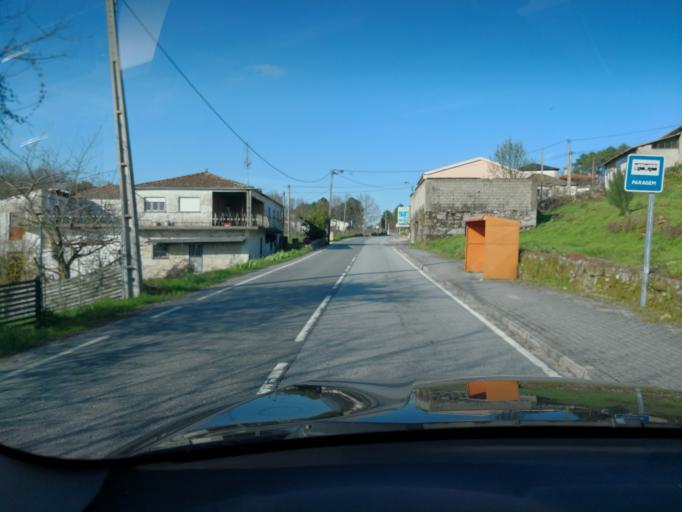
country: PT
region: Vila Real
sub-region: Vila Real
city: Vila Real
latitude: 41.3253
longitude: -7.6768
